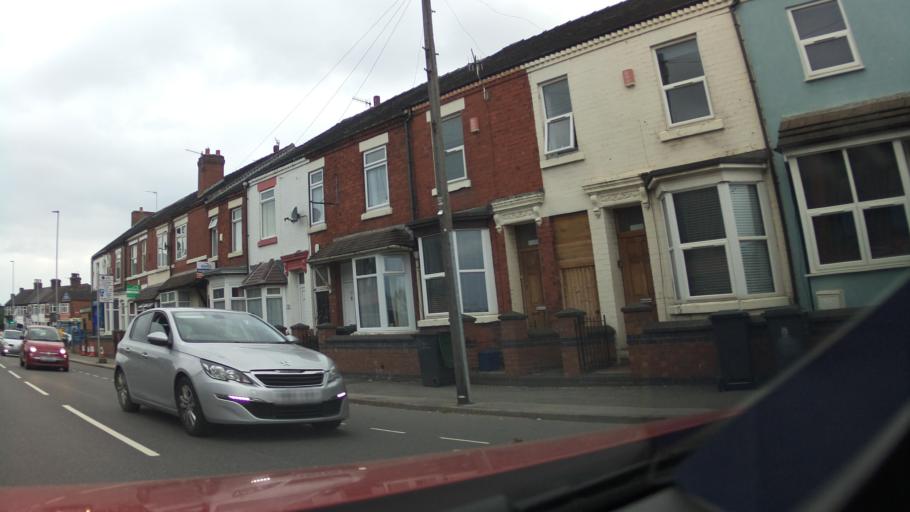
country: GB
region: England
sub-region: Stoke-on-Trent
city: Stoke-on-Trent
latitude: 53.0093
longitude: -2.1762
